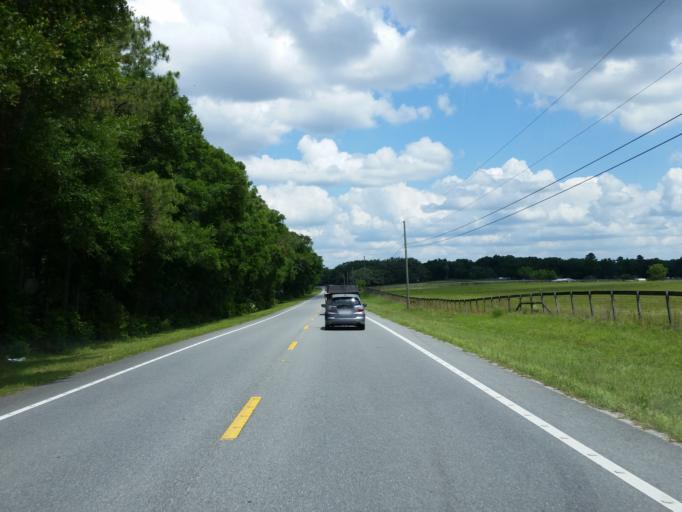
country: US
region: Florida
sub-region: Citrus County
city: Hernando
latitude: 28.9405
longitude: -82.4002
